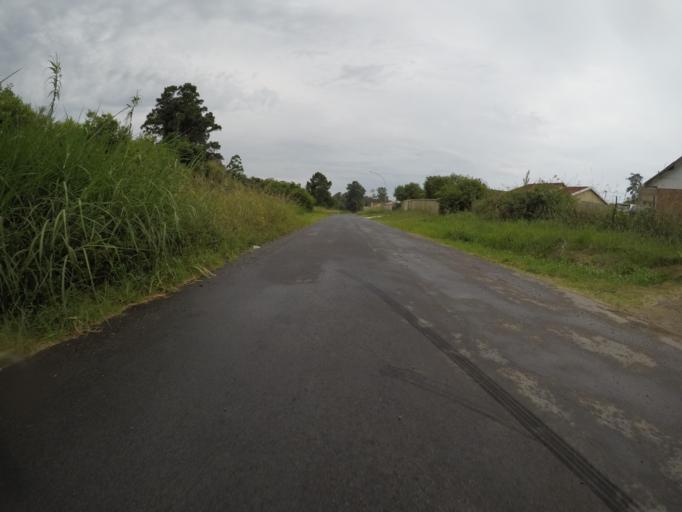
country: ZA
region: Eastern Cape
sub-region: Buffalo City Metropolitan Municipality
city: East London
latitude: -32.9657
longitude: 27.8339
